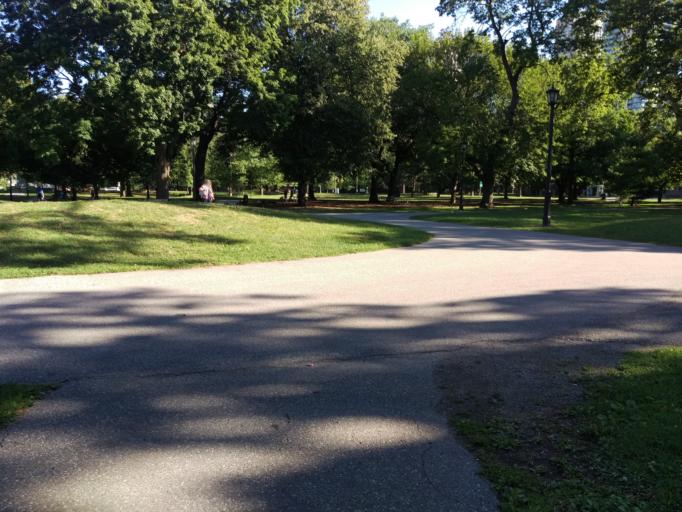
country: CA
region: Ontario
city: Toronto
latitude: 43.6642
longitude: -79.3923
